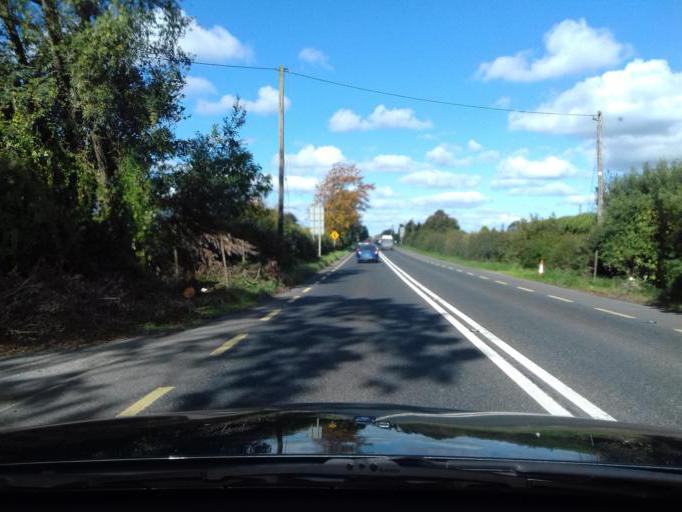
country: IE
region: Leinster
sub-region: An Mhi
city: Ratoath
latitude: 53.5628
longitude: -6.4431
